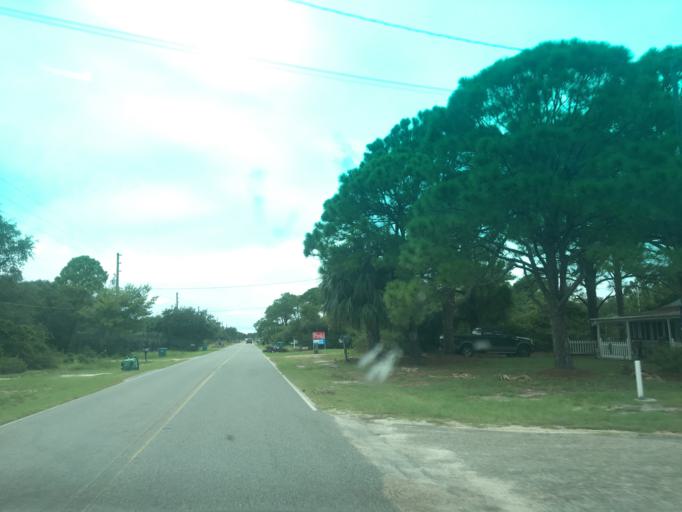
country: US
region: Florida
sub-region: Franklin County
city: Carrabelle
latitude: 29.8978
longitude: -84.3902
